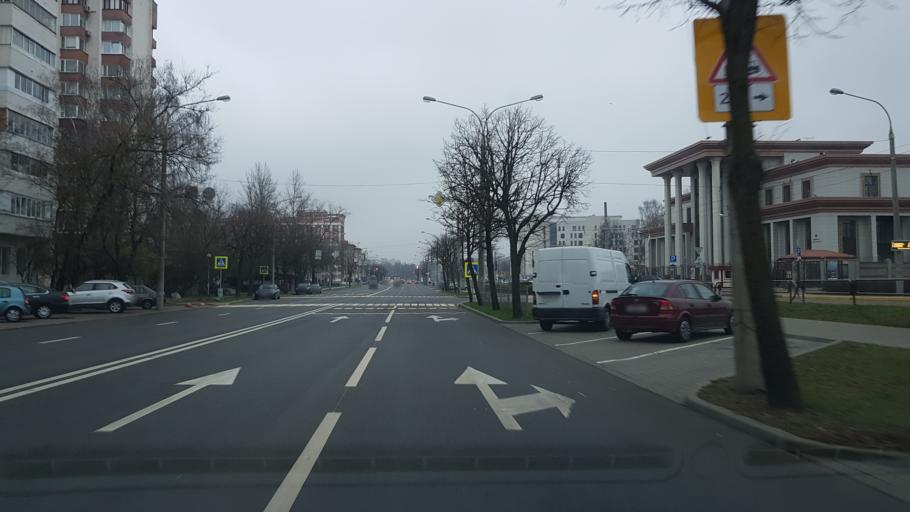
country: BY
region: Minsk
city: Minsk
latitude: 53.9250
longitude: 27.5460
